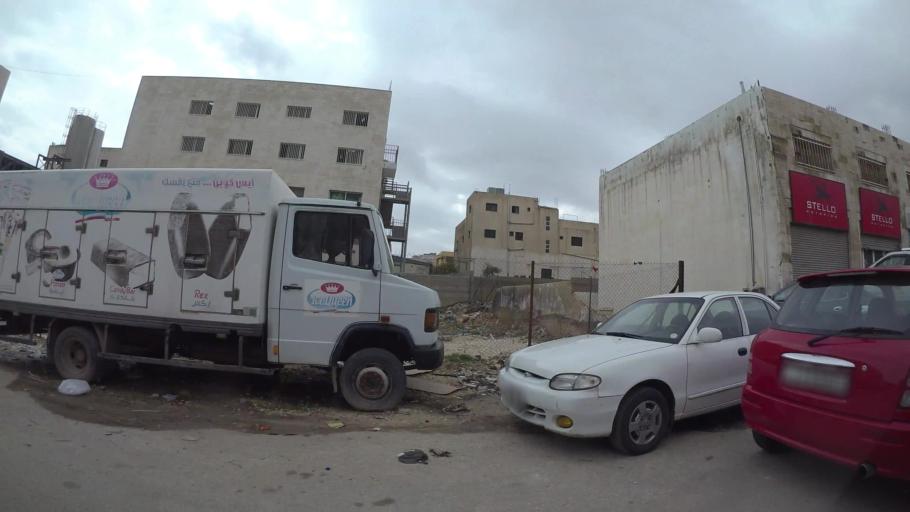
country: JO
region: Amman
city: Wadi as Sir
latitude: 31.9446
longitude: 35.8454
